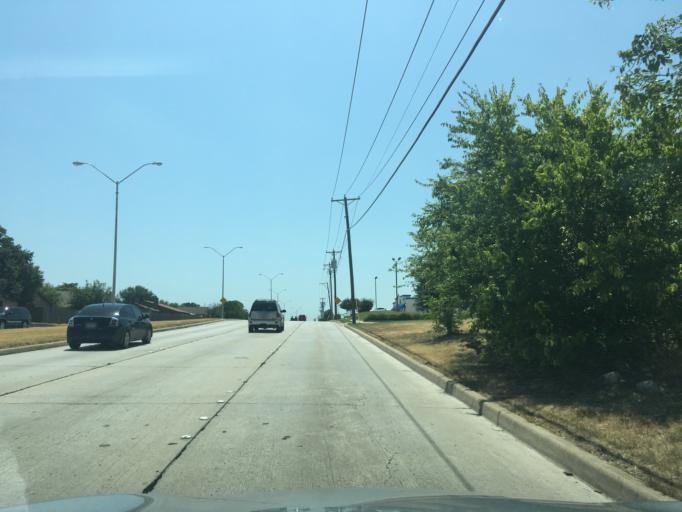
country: US
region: Texas
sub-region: Tarrant County
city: Edgecliff Village
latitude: 32.6407
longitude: -97.3698
